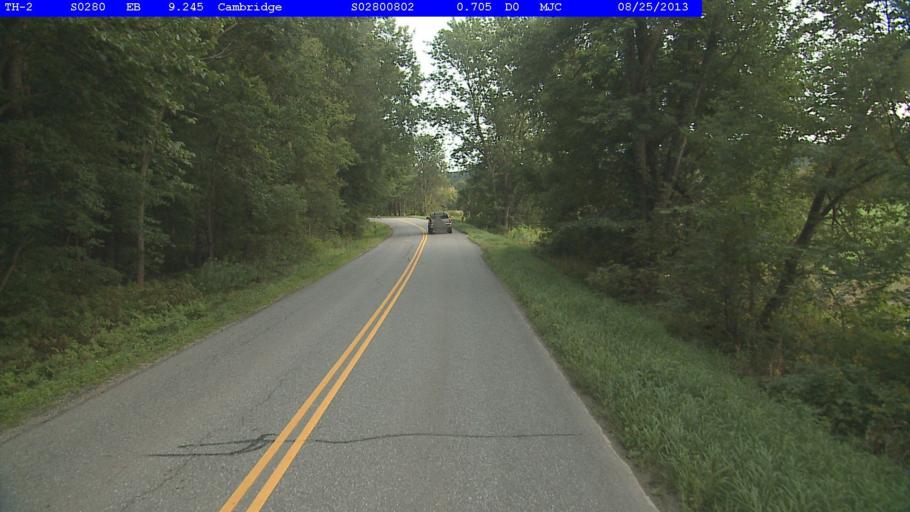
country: US
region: Vermont
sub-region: Chittenden County
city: Jericho
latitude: 44.6534
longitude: -72.8803
